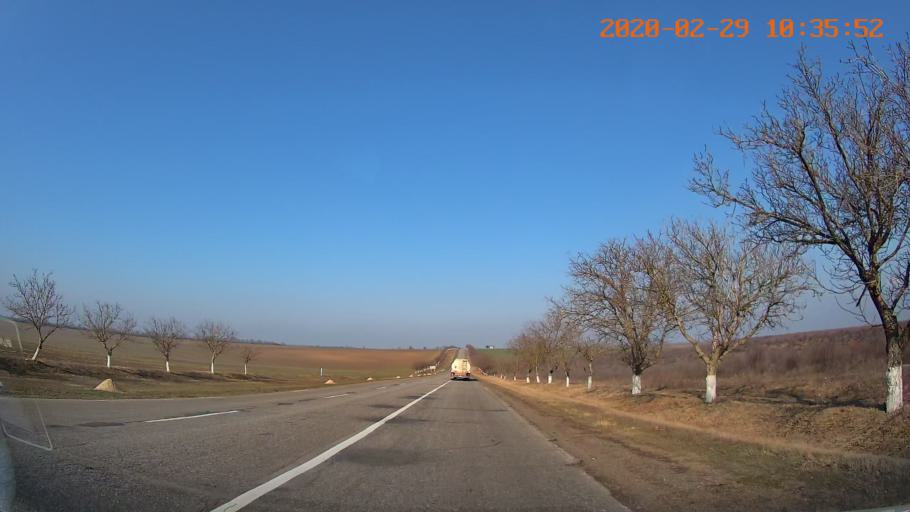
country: MD
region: Anenii Noi
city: Varnita
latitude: 46.9898
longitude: 29.5141
